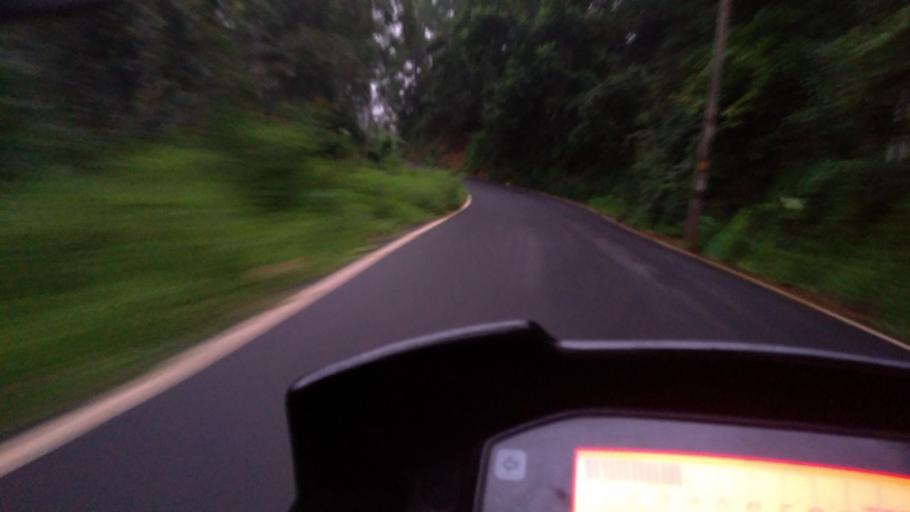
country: IN
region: Kerala
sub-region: Idukki
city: Munnar
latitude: 9.9558
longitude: 77.0830
